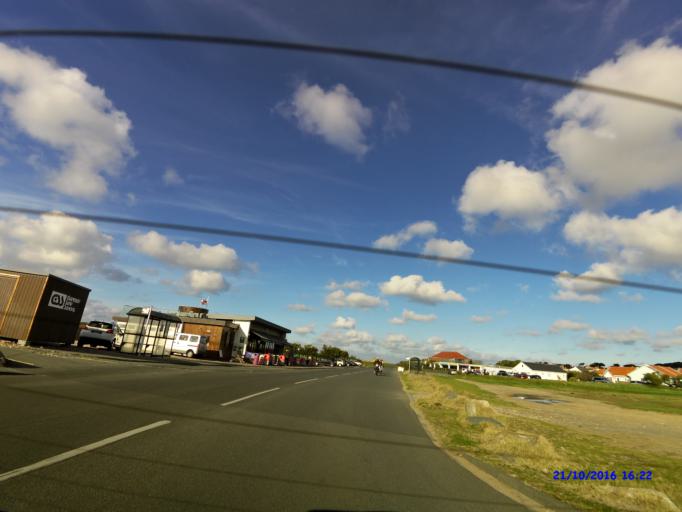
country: GG
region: St Peter Port
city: Saint Peter Port
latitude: 49.4702
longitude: -2.6060
